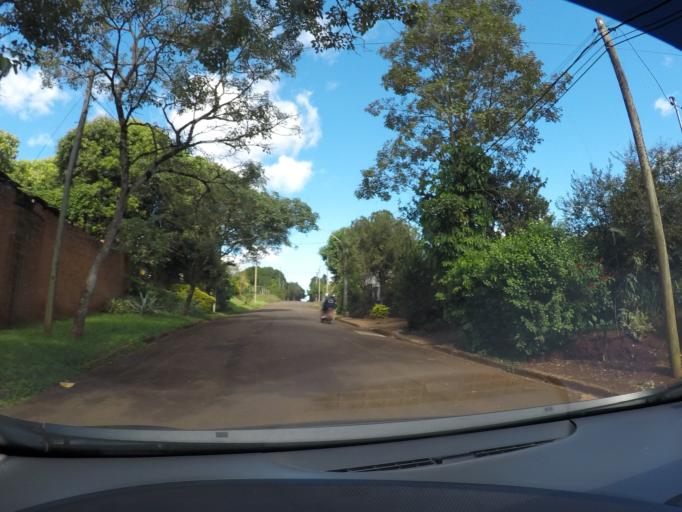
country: AR
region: Misiones
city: Puerto Rico
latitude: -26.8066
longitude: -55.0162
